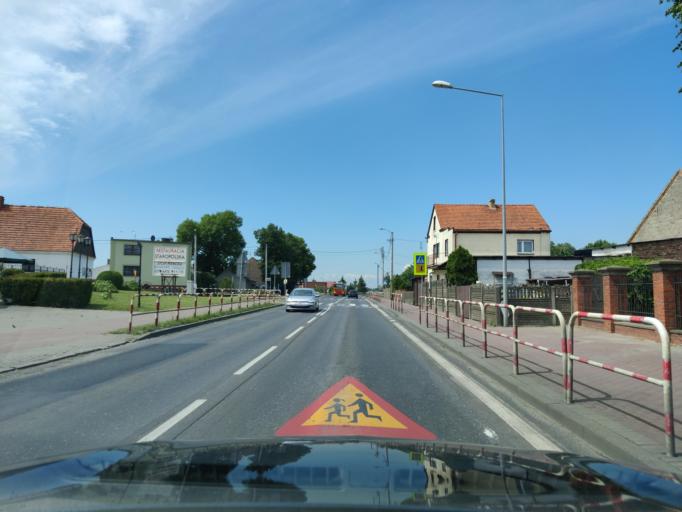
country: PL
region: Greater Poland Voivodeship
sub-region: Powiat grodziski
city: Kamieniec
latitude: 52.2262
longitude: 16.4392
